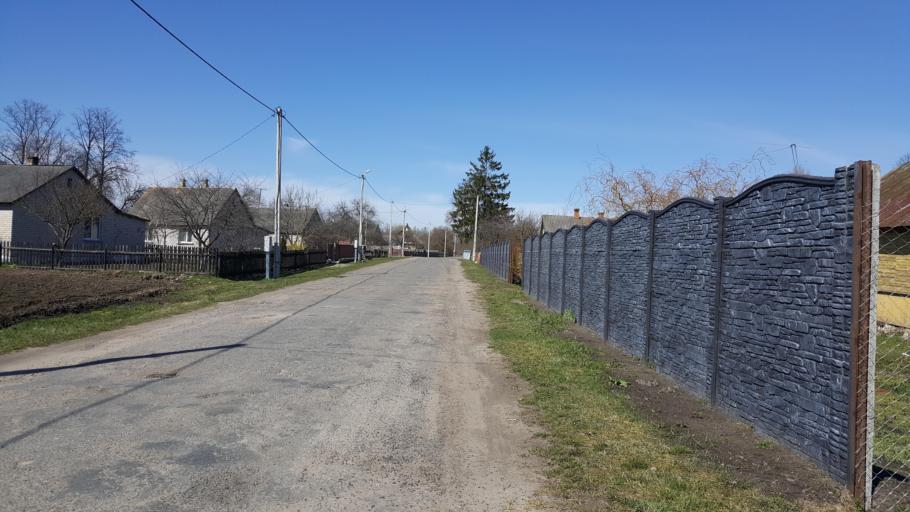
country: BY
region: Brest
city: Zhabinka
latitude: 52.2635
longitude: 23.9438
